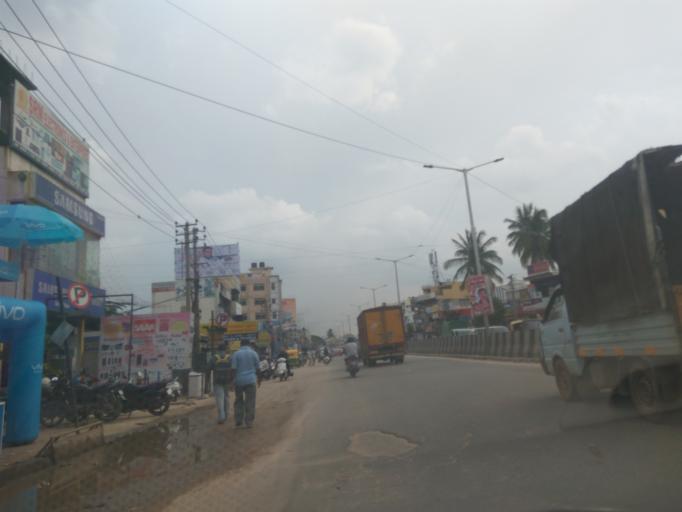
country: IN
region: Karnataka
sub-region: Bangalore Urban
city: Bangalore
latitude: 13.0103
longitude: 77.6977
